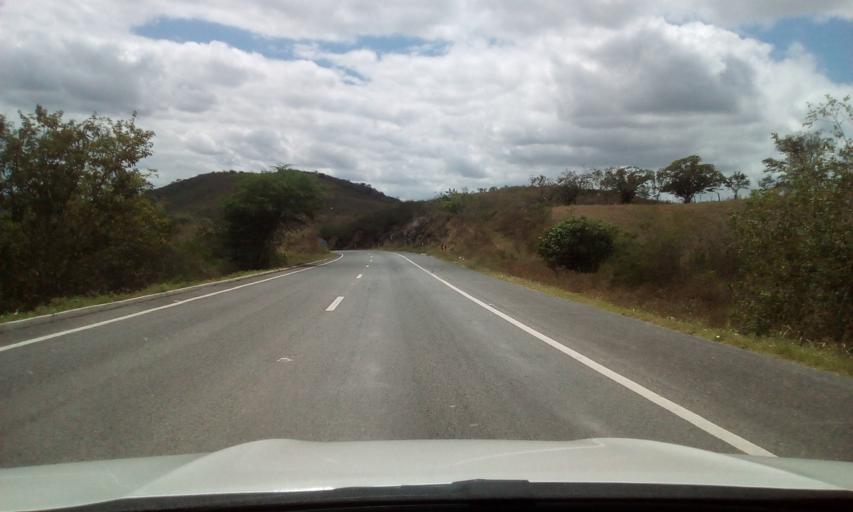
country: BR
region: Paraiba
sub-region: Inga
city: Inga
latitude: -7.2609
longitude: -35.6895
